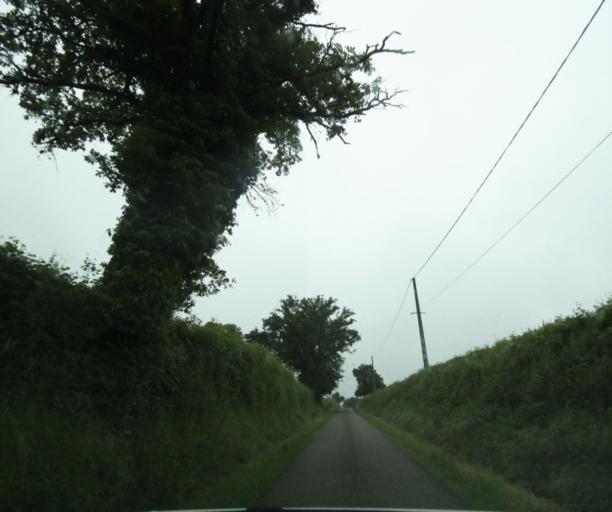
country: FR
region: Bourgogne
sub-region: Departement de Saone-et-Loire
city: Paray-le-Monial
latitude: 46.4110
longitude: 4.1815
